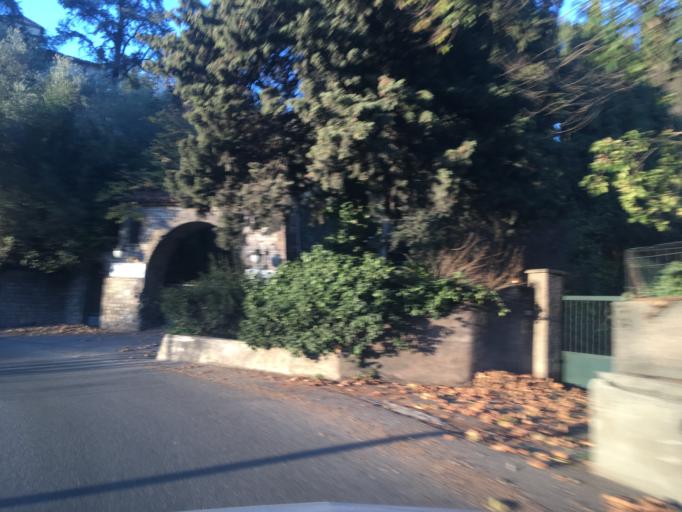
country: FR
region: Provence-Alpes-Cote d'Azur
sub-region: Departement des Alpes-Maritimes
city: Grasse
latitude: 43.6428
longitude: 6.9087
